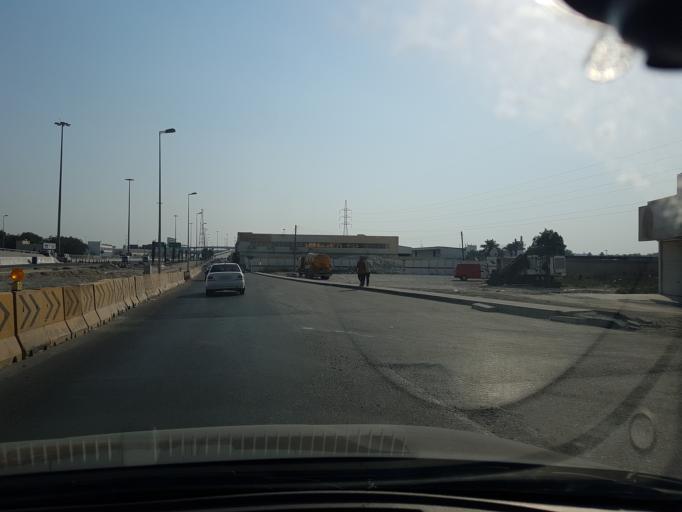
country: BH
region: Northern
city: Sitrah
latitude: 26.1300
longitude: 50.5993
